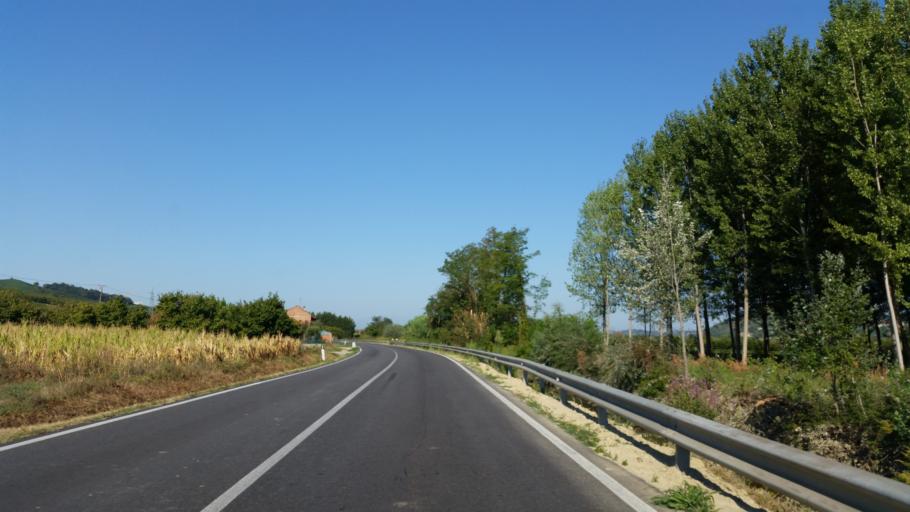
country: IT
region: Piedmont
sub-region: Provincia di Cuneo
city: Roddi
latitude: 44.6852
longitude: 7.9657
